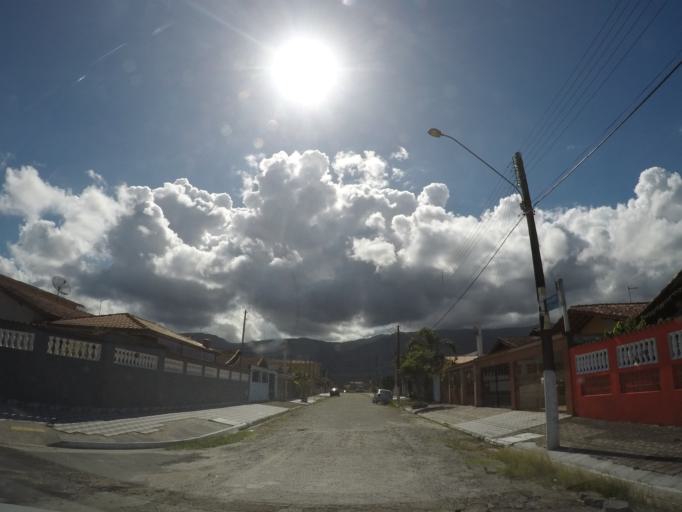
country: BR
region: Sao Paulo
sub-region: Mongagua
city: Mongagua
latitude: -24.0639
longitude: -46.5617
